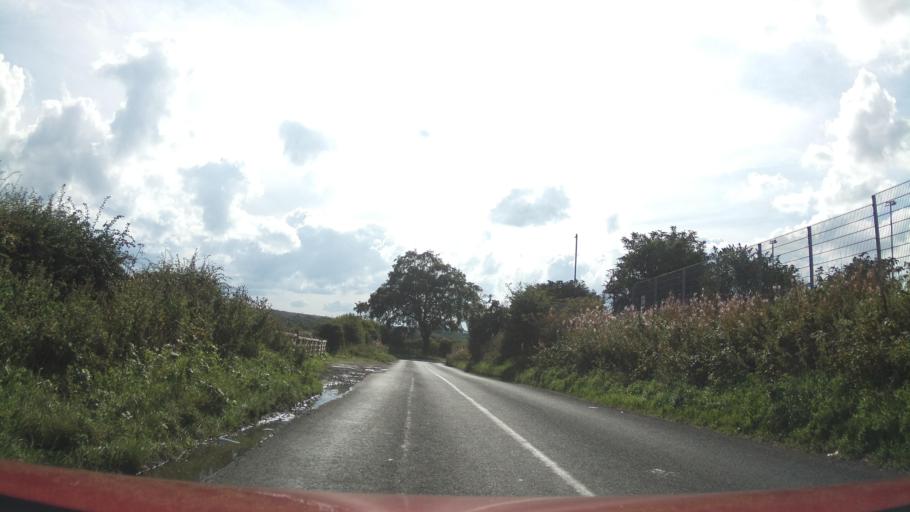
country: GB
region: Scotland
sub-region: Falkirk
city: Larbert
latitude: 56.0122
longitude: -3.8359
